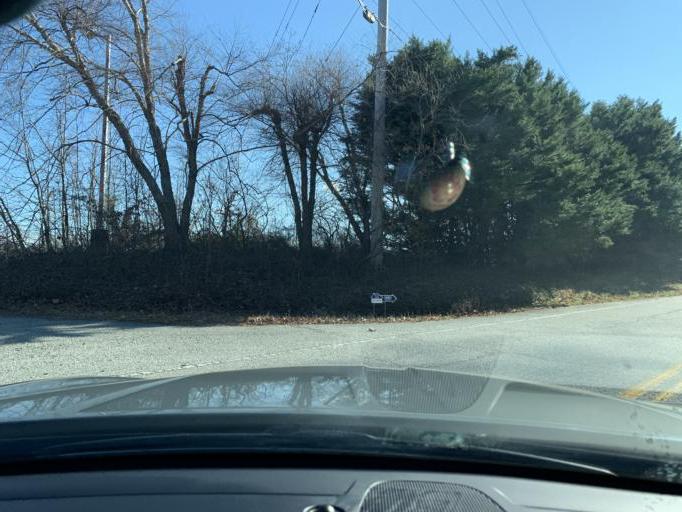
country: US
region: Maryland
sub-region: Queen Anne's County
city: Kingstown
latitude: 39.2642
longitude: -75.8665
